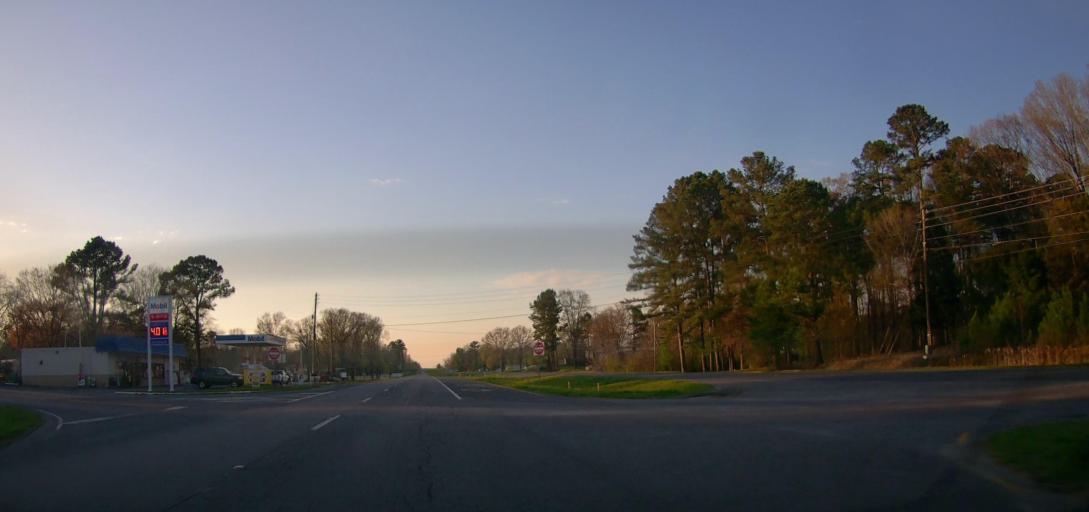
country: US
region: Alabama
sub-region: Talladega County
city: Childersburg
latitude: 33.2403
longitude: -86.3335
